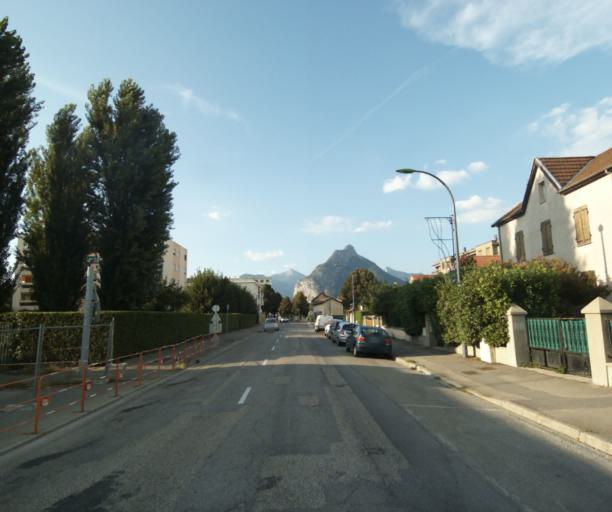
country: FR
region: Rhone-Alpes
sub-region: Departement de l'Isere
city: Seyssinet-Pariset
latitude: 45.1835
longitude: 5.6971
